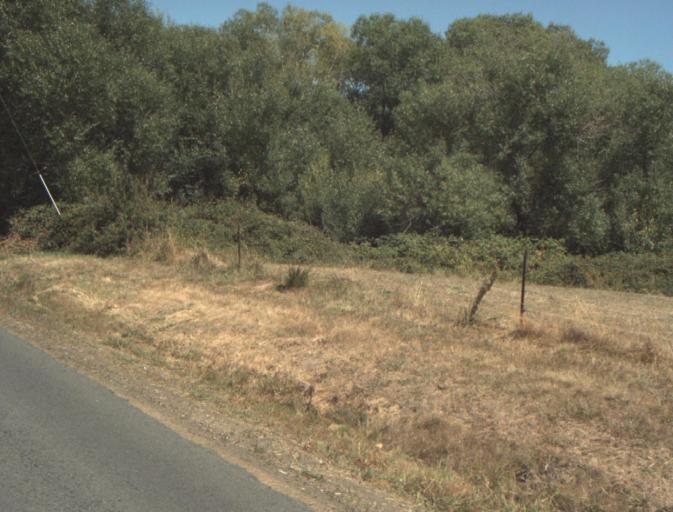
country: AU
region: Tasmania
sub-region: Launceston
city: Mayfield
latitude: -41.2599
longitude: 147.1359
